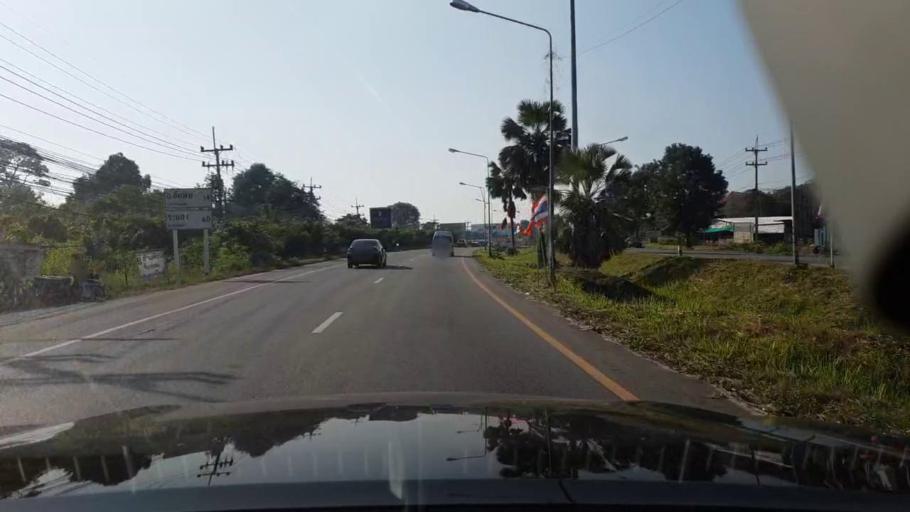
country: TH
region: Chon Buri
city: Sattahip
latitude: 12.7926
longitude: 100.9179
